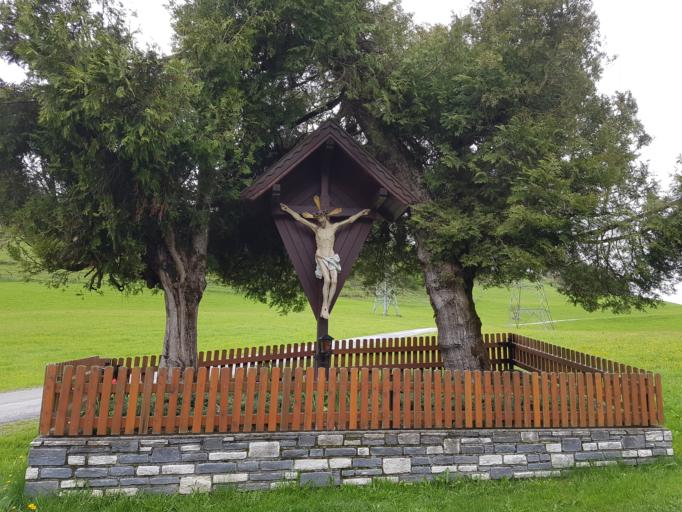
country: AT
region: Salzburg
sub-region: Politischer Bezirk Sankt Johann im Pongau
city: Schwarzach im Pongau
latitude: 47.3244
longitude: 13.1332
